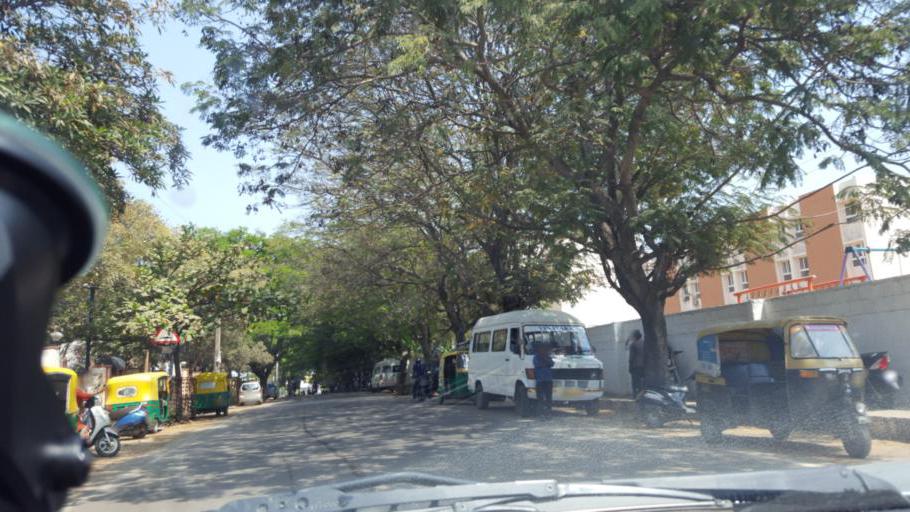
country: IN
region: Karnataka
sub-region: Bangalore Urban
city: Bangalore
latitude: 12.9726
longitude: 77.6682
